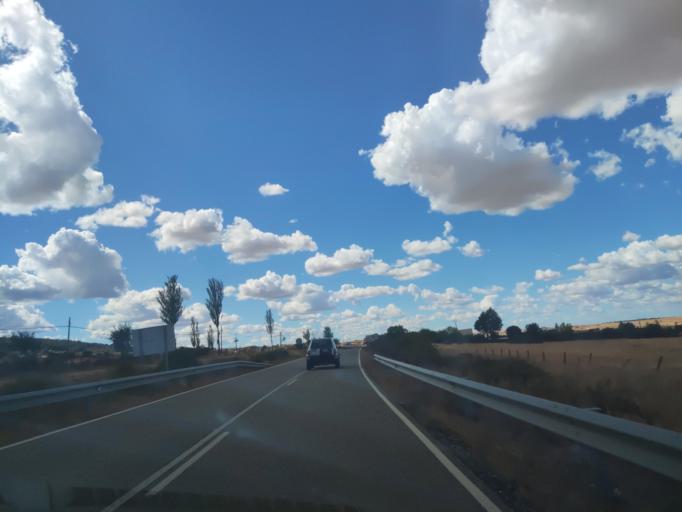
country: ES
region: Castille and Leon
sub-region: Provincia de Salamanca
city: Tamames
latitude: 40.6536
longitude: -6.0969
